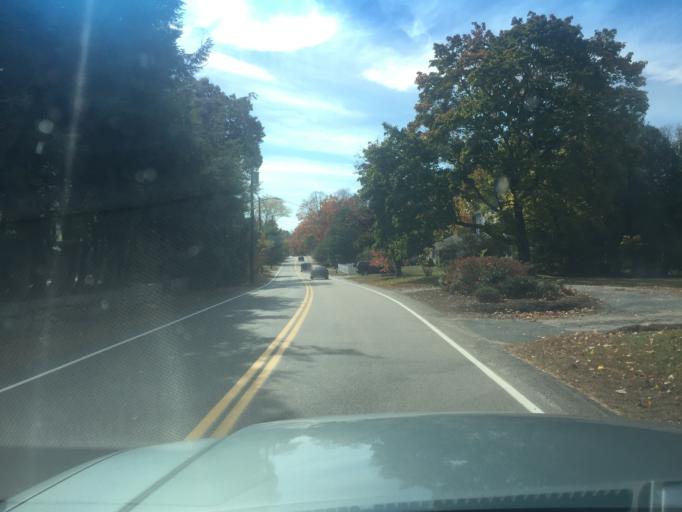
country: US
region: Massachusetts
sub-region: Norfolk County
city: Medway
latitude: 42.1514
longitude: -71.4257
